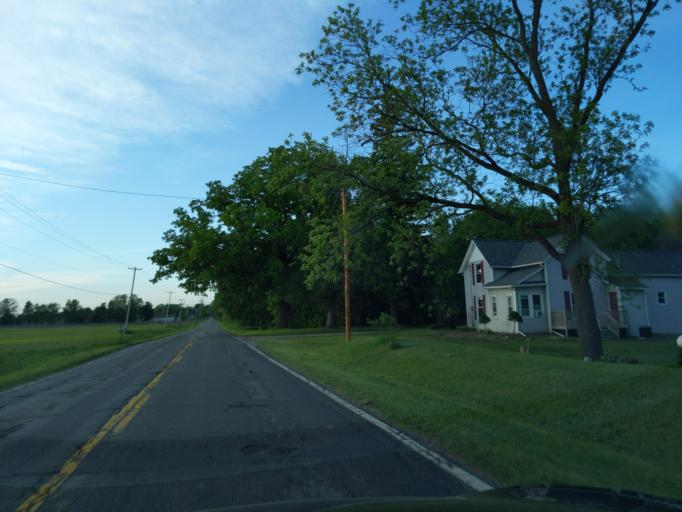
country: US
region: Michigan
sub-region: Ingham County
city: Mason
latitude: 42.5442
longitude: -84.3028
